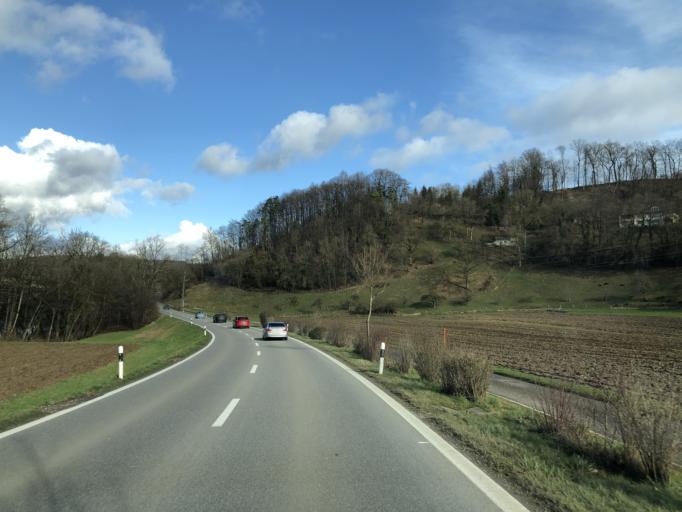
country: CH
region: Aargau
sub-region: Bezirk Baden
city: Gebenstorf
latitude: 47.4710
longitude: 8.2347
